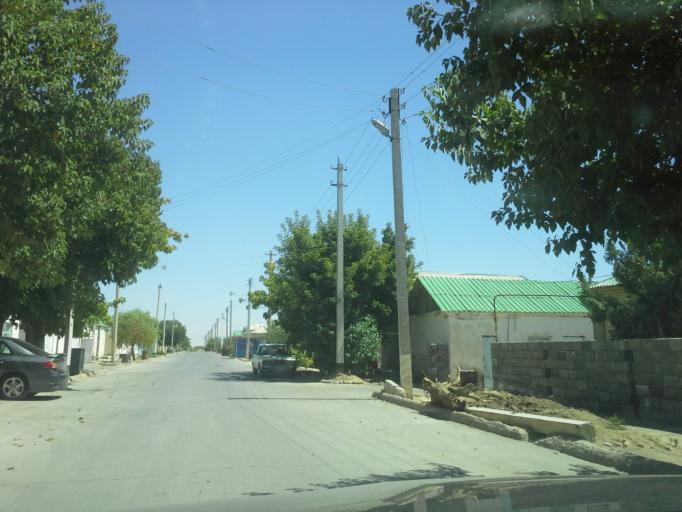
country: TM
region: Ahal
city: Abadan
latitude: 38.0413
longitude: 58.2275
